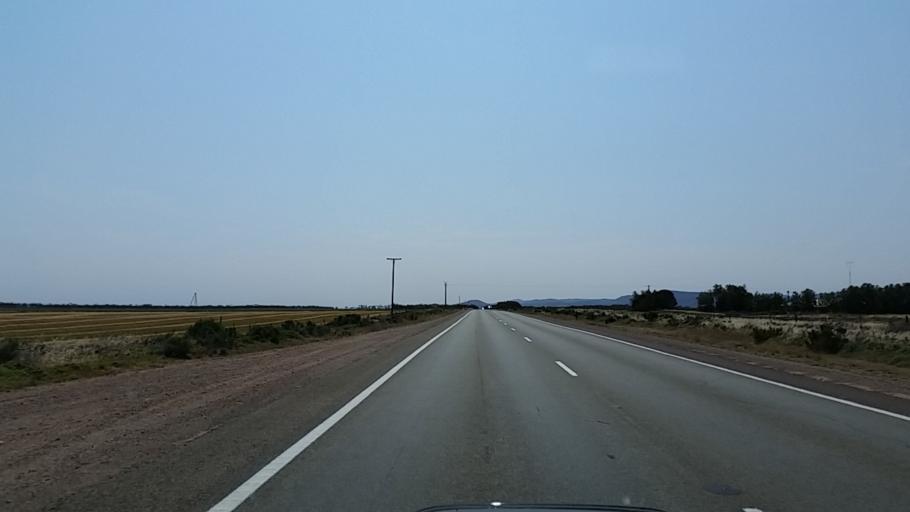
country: AU
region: South Australia
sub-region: Port Pirie City and Dists
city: Port Pirie
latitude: -32.9589
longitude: 137.9825
